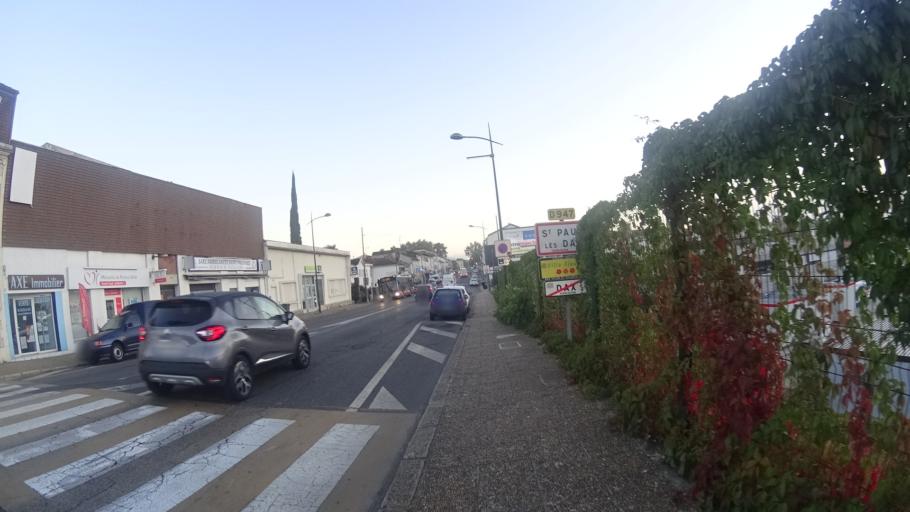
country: FR
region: Aquitaine
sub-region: Departement des Landes
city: Saint-Paul-les-Dax
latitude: 43.7210
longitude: -1.0521
